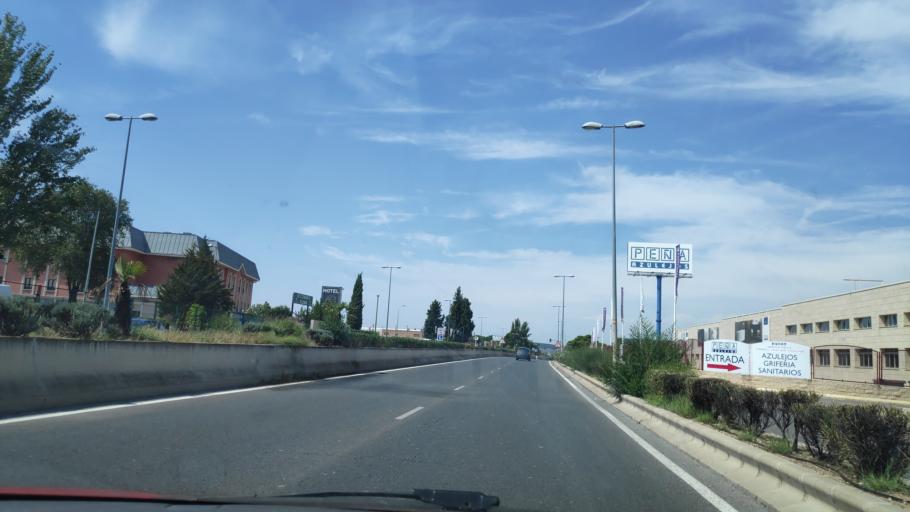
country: ES
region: Madrid
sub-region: Provincia de Madrid
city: Arganda
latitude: 40.3069
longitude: -3.4667
